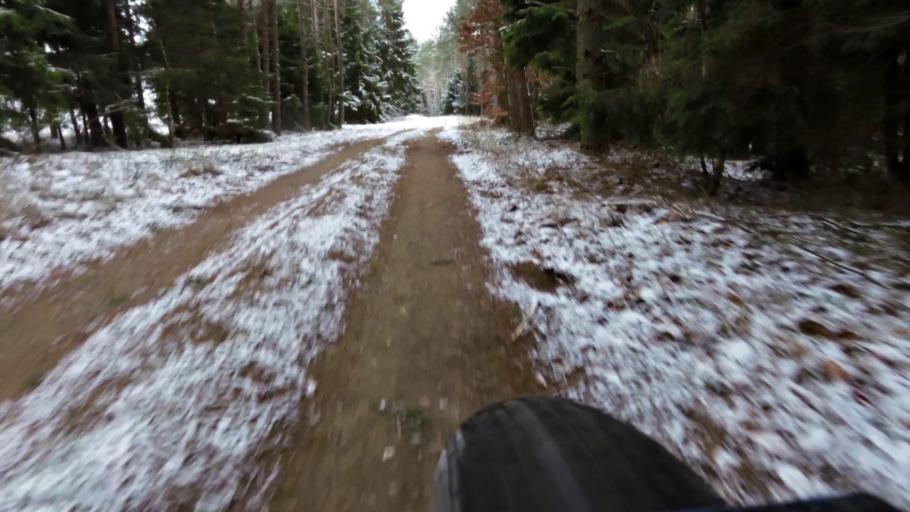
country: PL
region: West Pomeranian Voivodeship
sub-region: Powiat walecki
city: Miroslawiec
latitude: 53.3735
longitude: 16.1673
